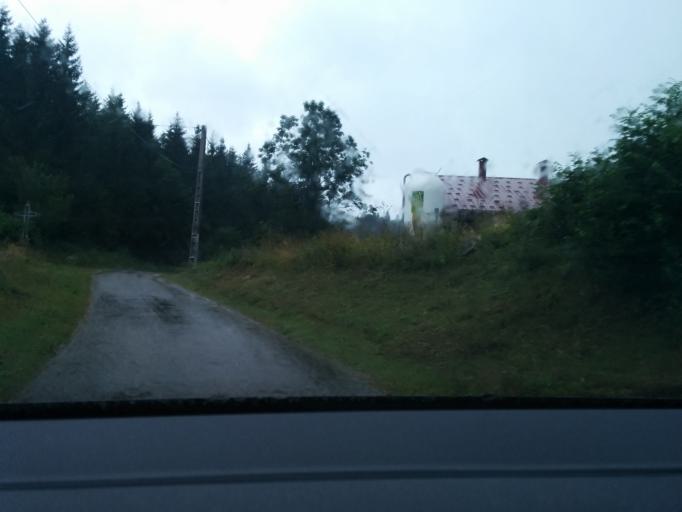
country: FR
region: Franche-Comte
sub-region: Departement du Jura
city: Valfin-les-Saint-Claude
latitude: 46.4634
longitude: 5.8368
